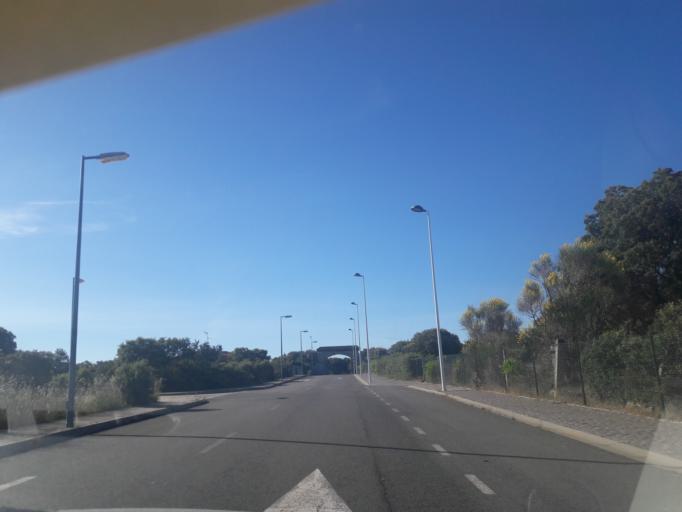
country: ES
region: Castille and Leon
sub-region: Provincia de Salamanca
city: Martinamor
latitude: 40.8077
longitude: -5.6443
